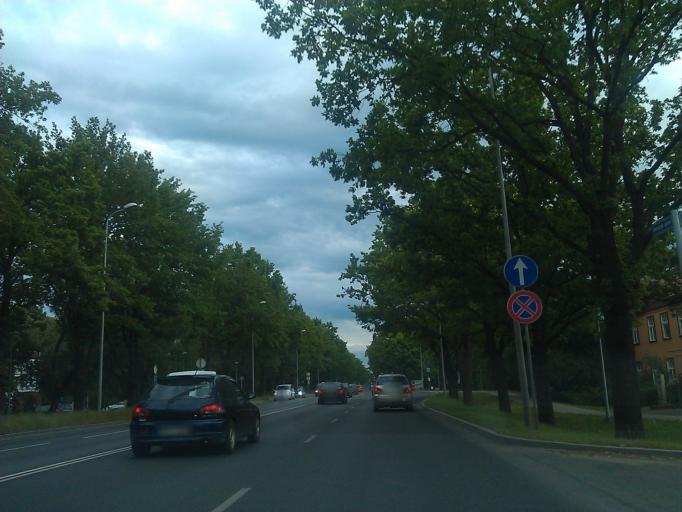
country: LV
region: Marupe
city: Marupe
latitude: 56.9055
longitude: 24.0826
